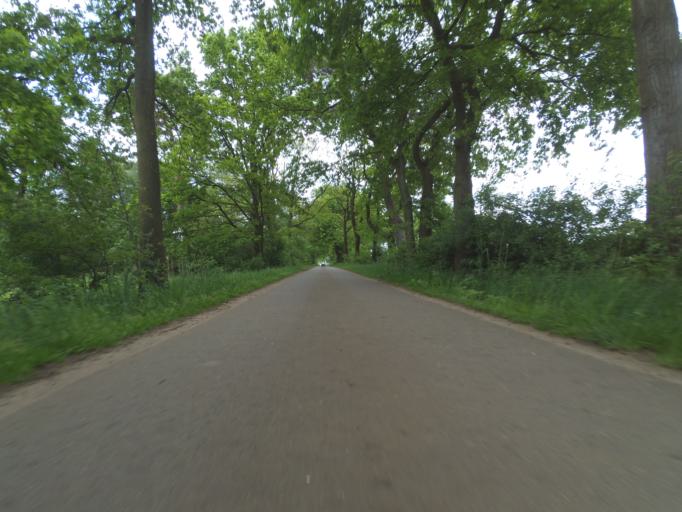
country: DE
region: Lower Saxony
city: Wietze
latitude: 52.6186
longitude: 9.8122
